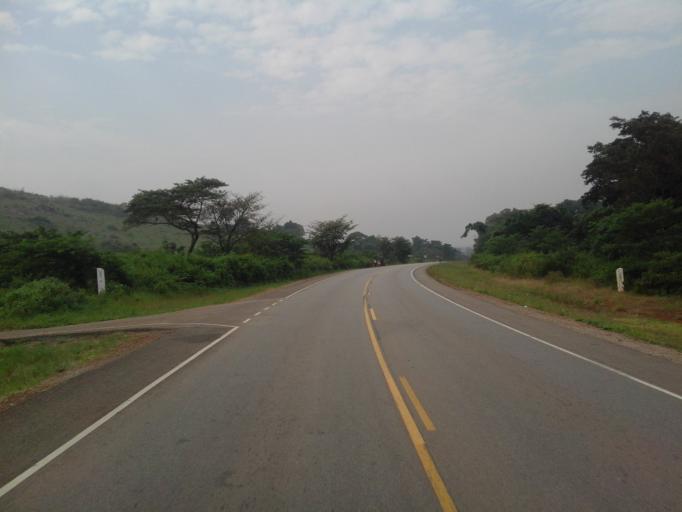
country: UG
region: Eastern Region
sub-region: Busia District
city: Busia
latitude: 0.5456
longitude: 34.0164
